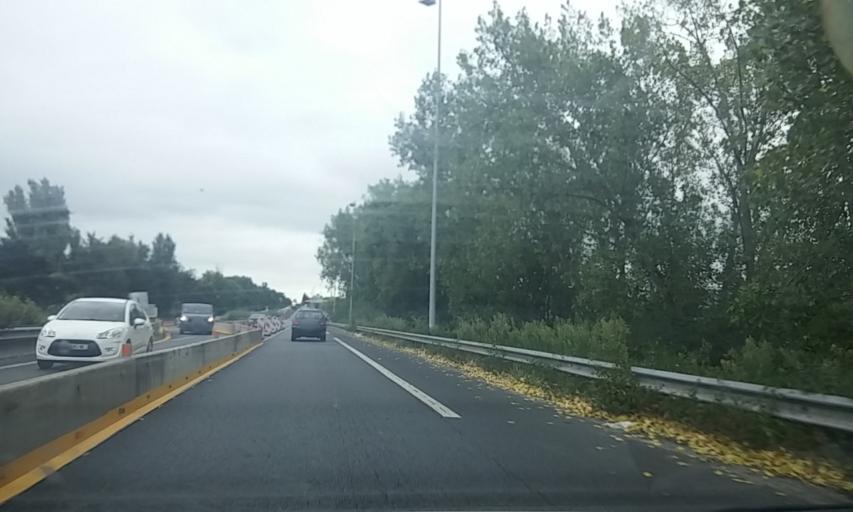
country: FR
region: Ile-de-France
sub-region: Departement du Val-de-Marne
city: Rungis
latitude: 48.7530
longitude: 2.3531
